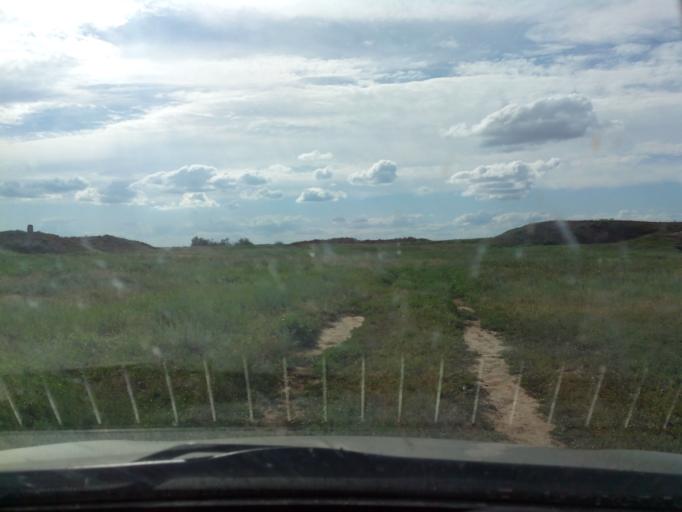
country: RU
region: Volgograd
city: Leninsk
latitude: 48.6807
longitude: 45.3692
